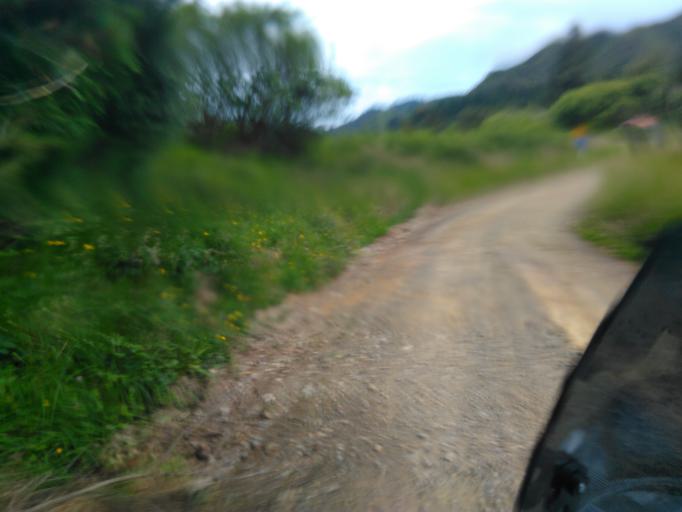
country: NZ
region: Bay of Plenty
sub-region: Opotiki District
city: Opotiki
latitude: -38.1105
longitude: 177.5072
